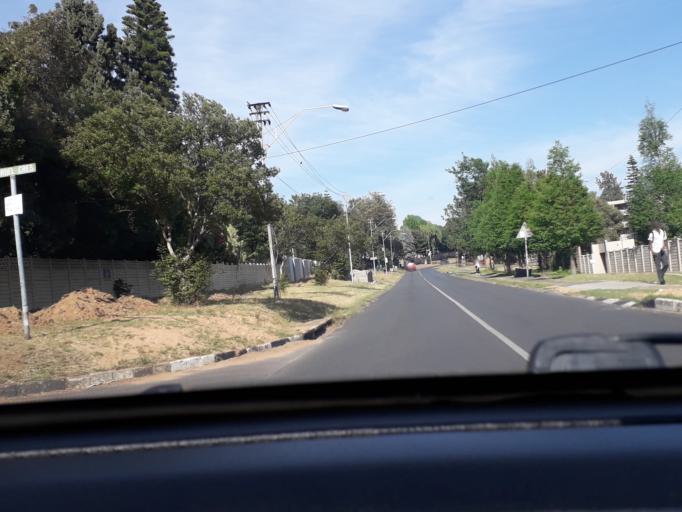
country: ZA
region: Gauteng
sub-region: City of Johannesburg Metropolitan Municipality
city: Modderfontein
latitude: -26.1383
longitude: 28.1021
